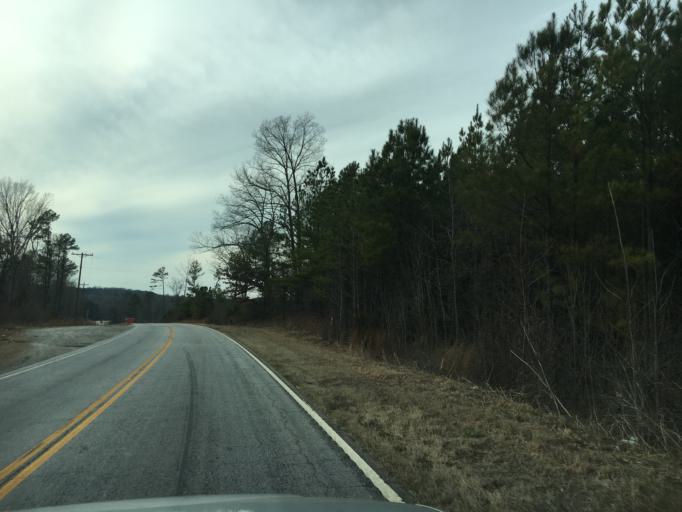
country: US
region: South Carolina
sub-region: Laurens County
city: Clinton
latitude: 34.5031
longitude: -81.8152
